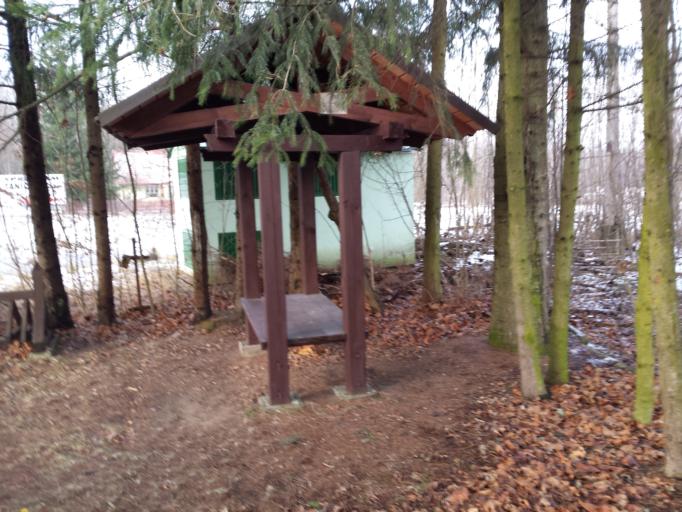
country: PL
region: Podlasie
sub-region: Powiat hajnowski
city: Bialowieza
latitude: 52.6946
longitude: 23.8282
